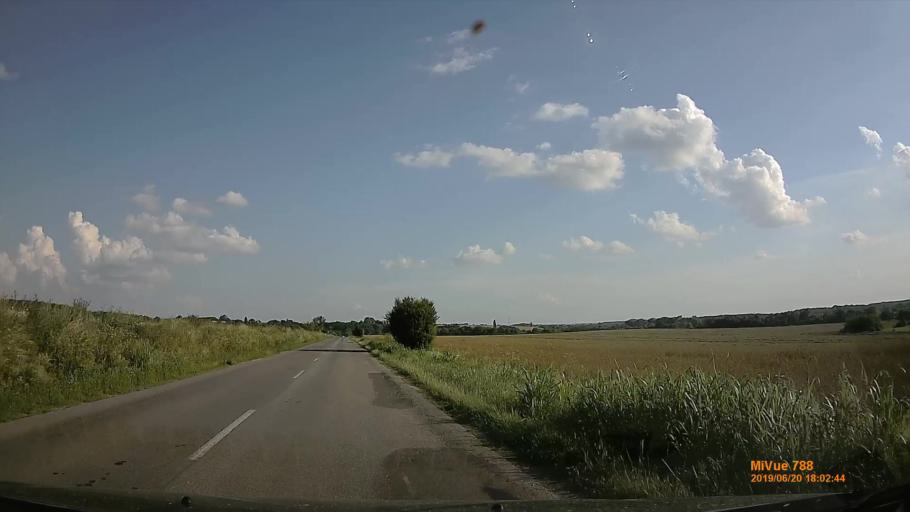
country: HU
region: Baranya
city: Szentlorinc
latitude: 46.0711
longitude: 17.9907
